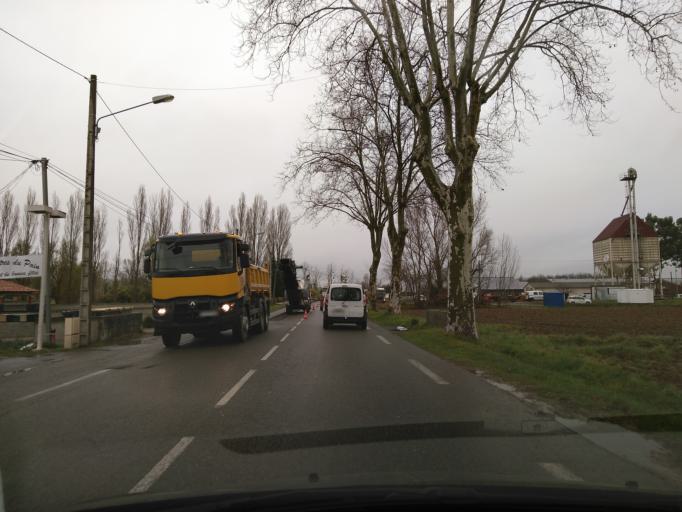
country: FR
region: Midi-Pyrenees
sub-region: Departement de la Haute-Garonne
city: Rieux-Volvestre
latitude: 43.2642
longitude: 1.1942
